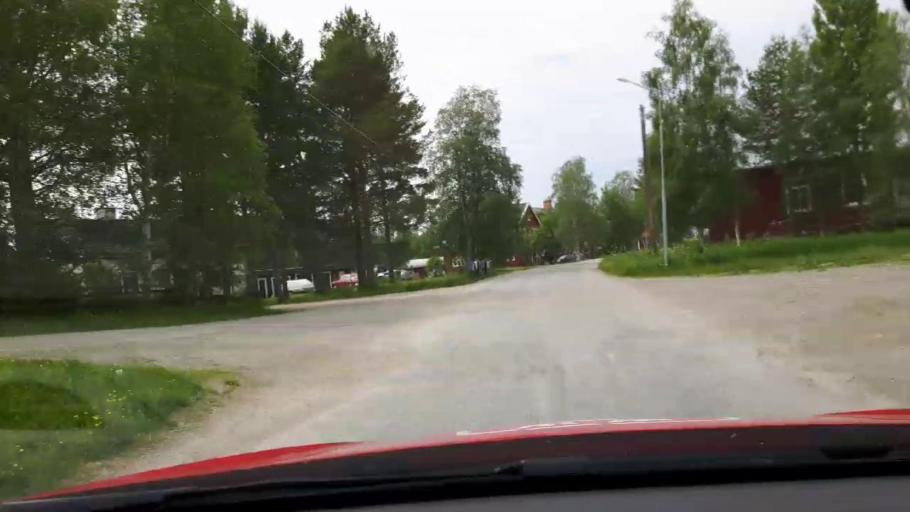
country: SE
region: Jaemtland
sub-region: Harjedalens Kommun
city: Sveg
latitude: 62.4086
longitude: 13.6774
